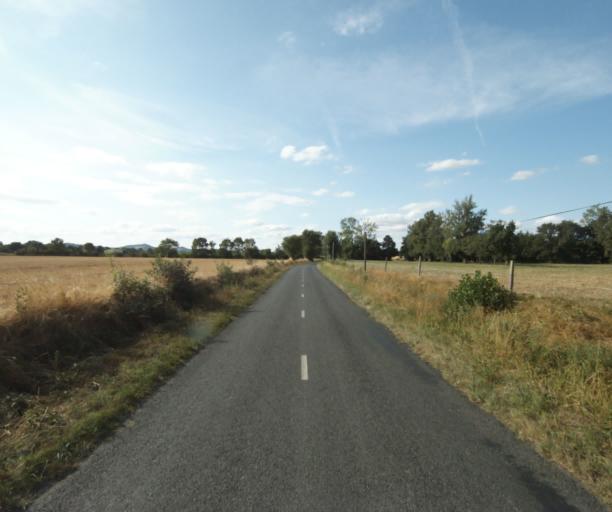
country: FR
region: Midi-Pyrenees
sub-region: Departement de la Haute-Garonne
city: Revel
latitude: 43.4788
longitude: 1.9902
